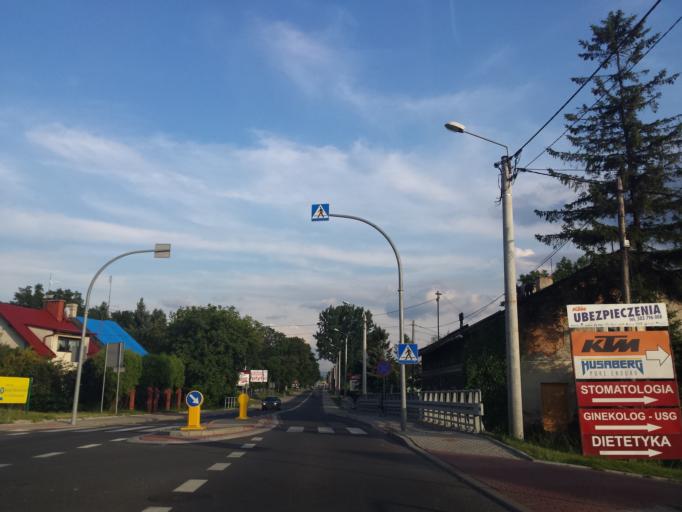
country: PL
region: Silesian Voivodeship
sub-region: Bielsko-Biala
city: Bielsko-Biala
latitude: 49.7965
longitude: 19.0640
